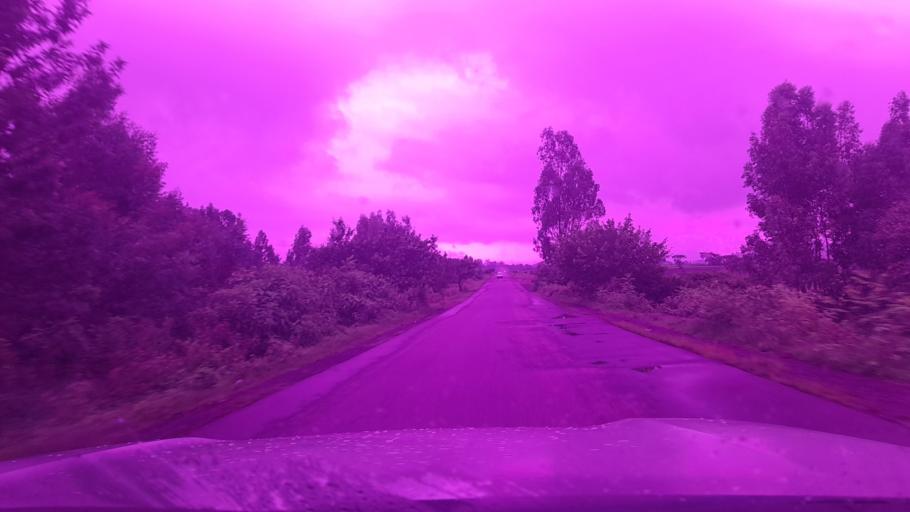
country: ET
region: Oromiya
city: Jima
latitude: 7.7810
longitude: 37.3423
